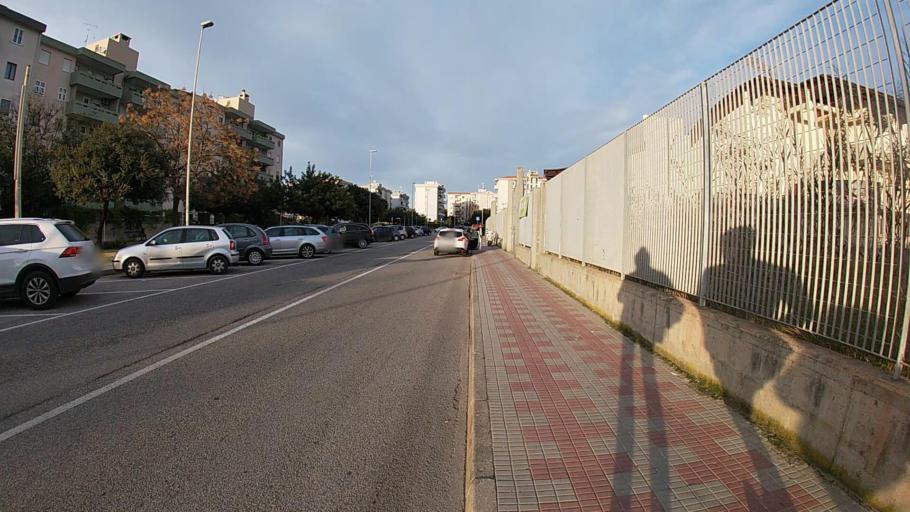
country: IT
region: Sardinia
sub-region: Provincia di Cagliari
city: Su Planu
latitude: 39.2413
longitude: 9.1034
